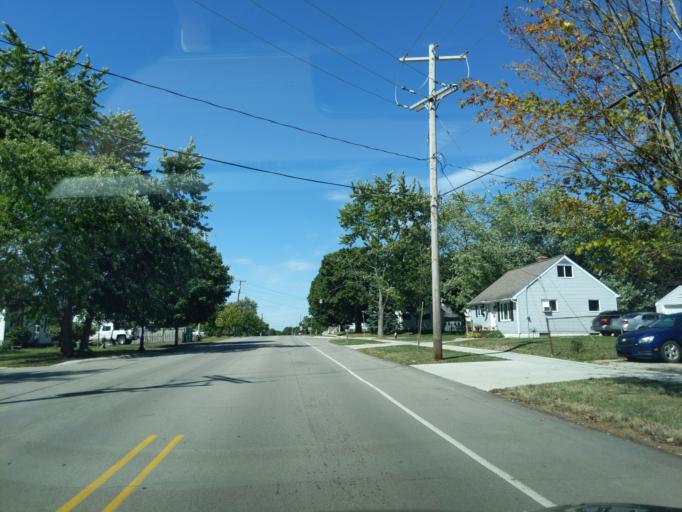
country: US
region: Michigan
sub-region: Eaton County
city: Potterville
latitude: 42.6257
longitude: -84.7447
